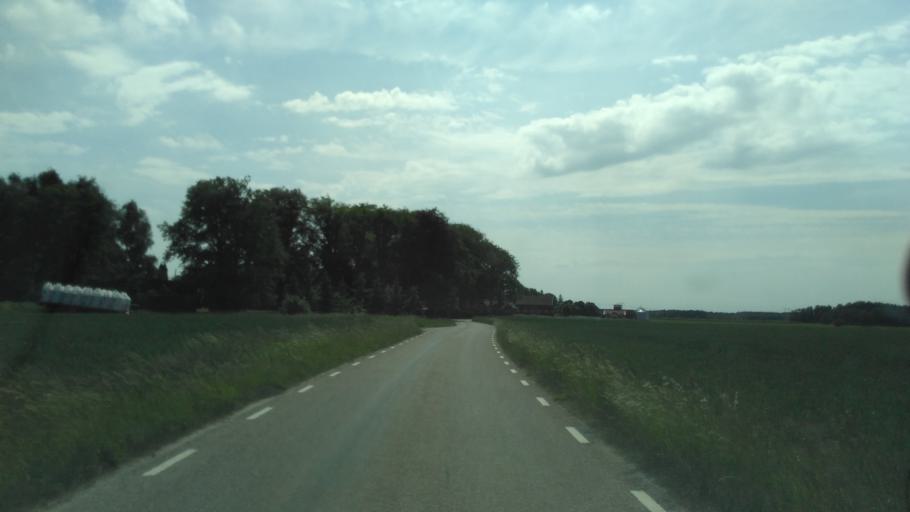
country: SE
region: Vaestra Goetaland
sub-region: Grastorps Kommun
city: Graestorp
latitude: 58.3920
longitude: 12.7924
